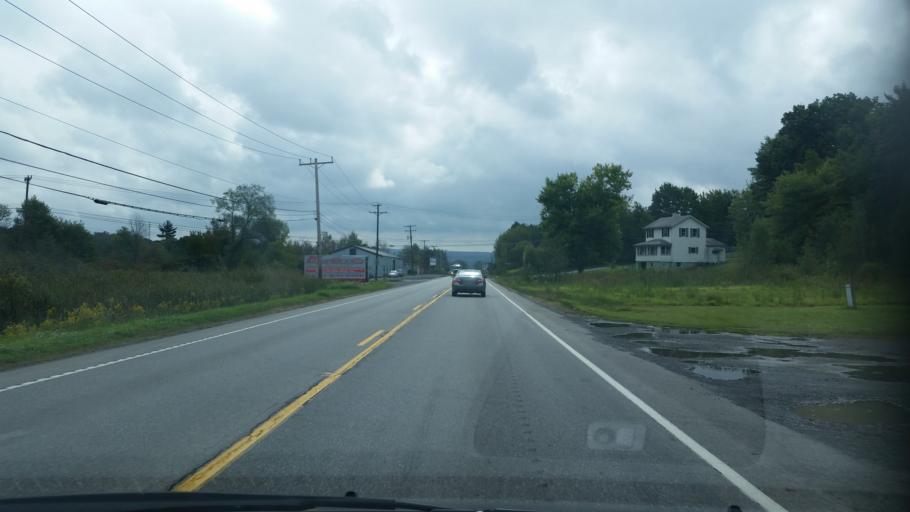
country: US
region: Pennsylvania
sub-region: Clearfield County
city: Troy
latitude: 40.9149
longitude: -78.2485
